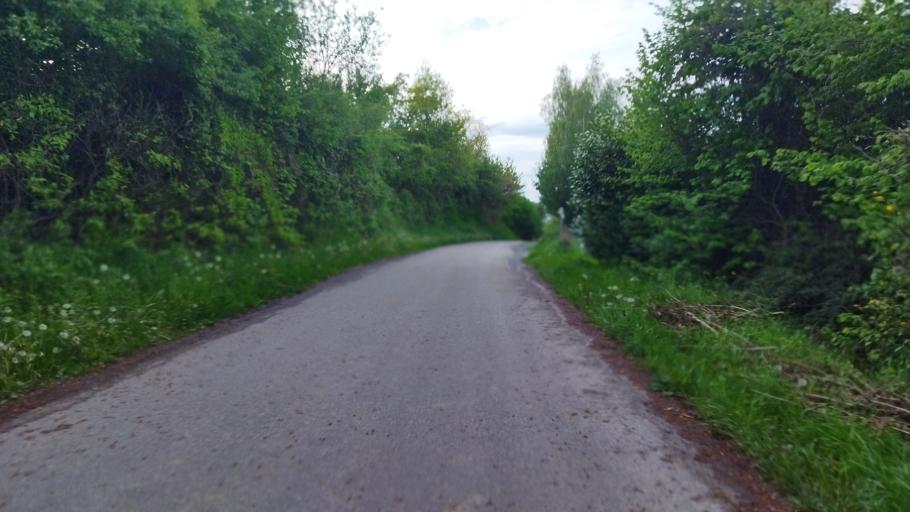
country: DE
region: Baden-Wuerttemberg
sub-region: Regierungsbezirk Stuttgart
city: Flein
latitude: 49.0963
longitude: 9.2277
